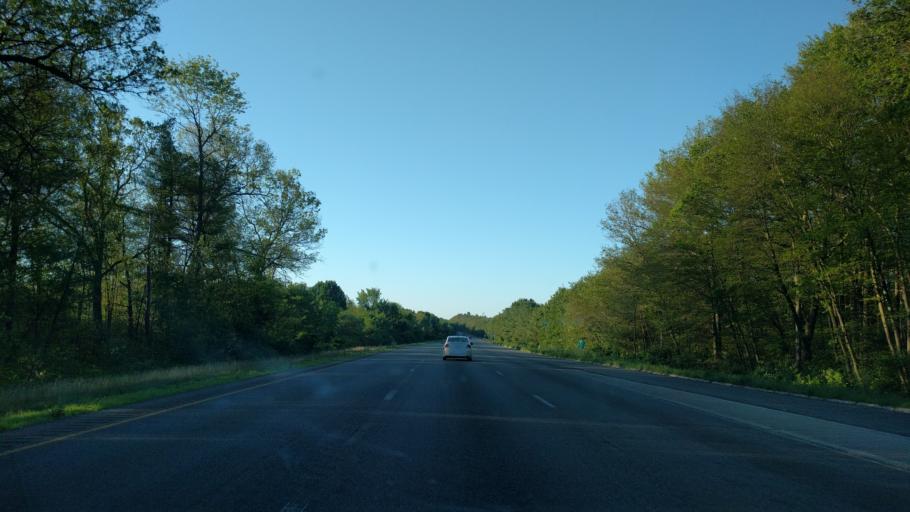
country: US
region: Massachusetts
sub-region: Middlesex County
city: Hopkinton
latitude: 42.2100
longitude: -71.5444
